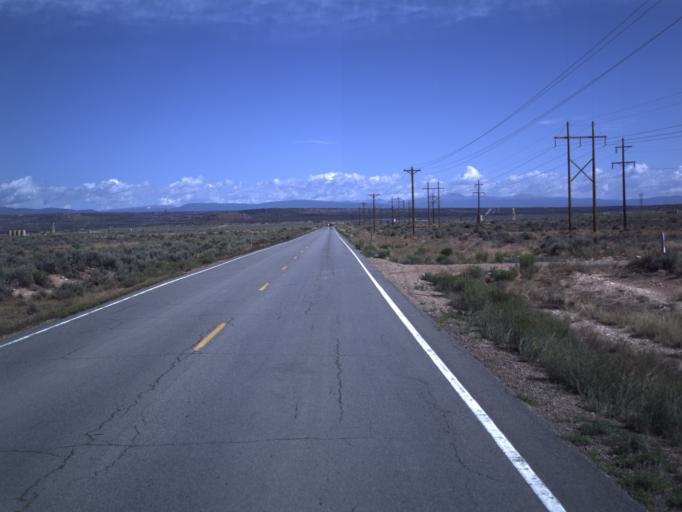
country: US
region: Utah
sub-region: Duchesne County
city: Duchesne
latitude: 40.2304
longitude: -110.3893
